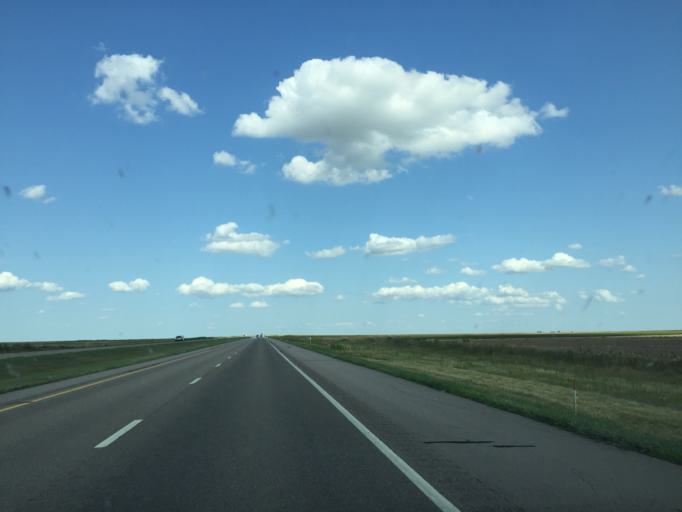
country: US
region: Kansas
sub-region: Trego County
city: WaKeeney
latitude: 39.0230
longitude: -100.0373
